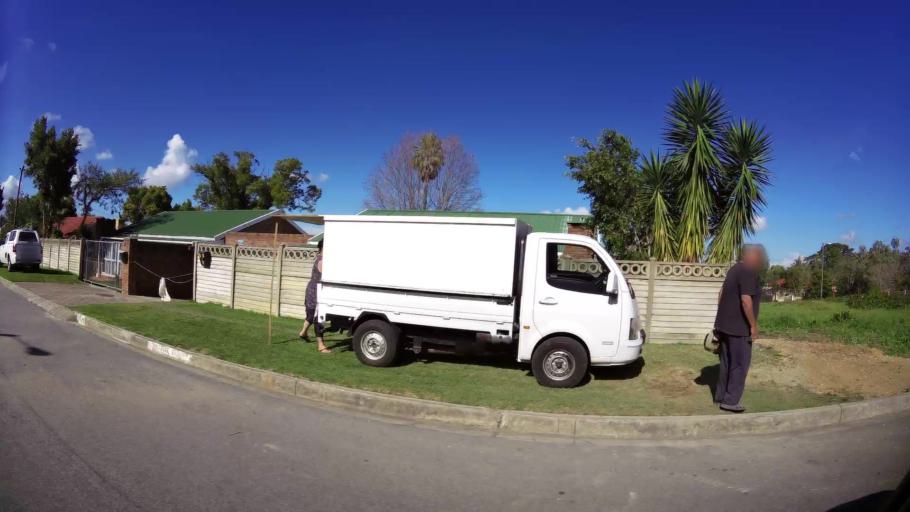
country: ZA
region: Western Cape
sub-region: Eden District Municipality
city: George
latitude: -33.9393
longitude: 22.4741
